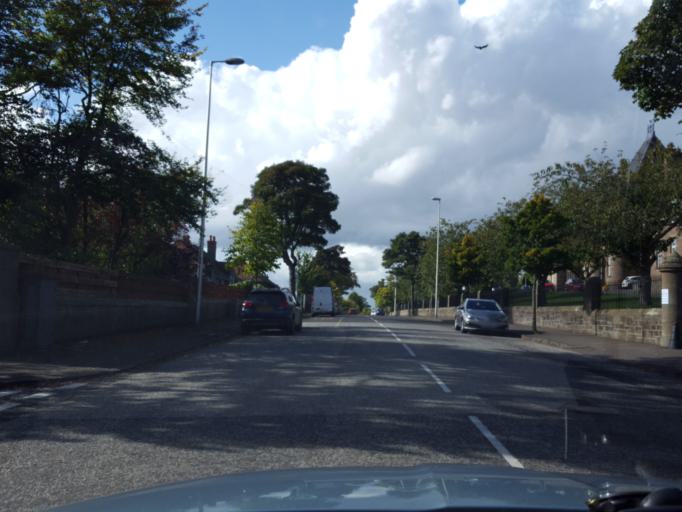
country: GB
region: Scotland
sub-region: Dundee City
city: Dundee
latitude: 56.4606
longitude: -3.0072
